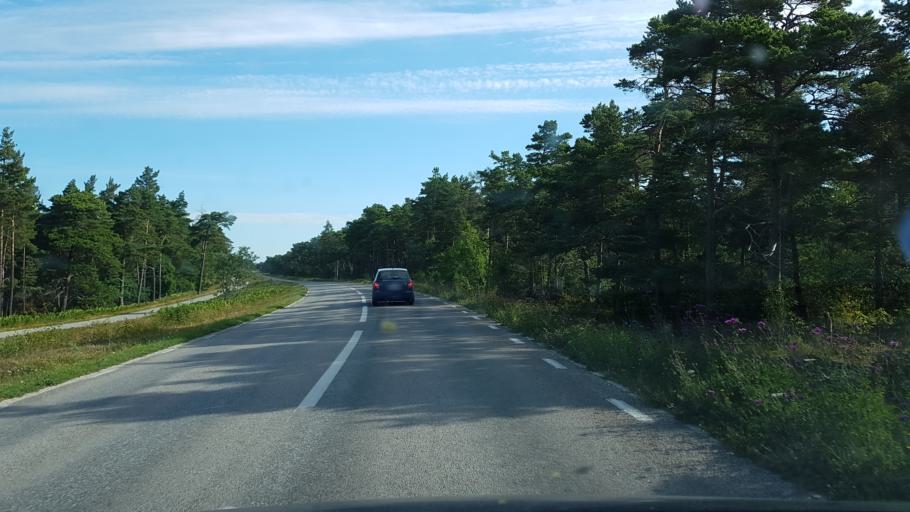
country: SE
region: Gotland
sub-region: Gotland
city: Visby
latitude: 57.7259
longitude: 18.4034
